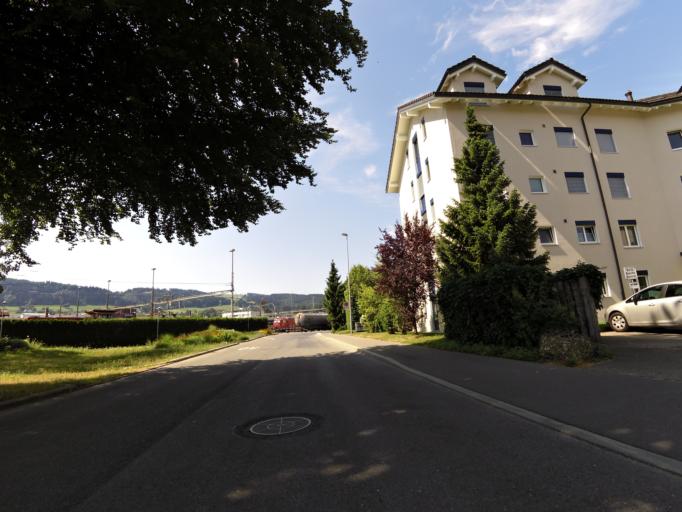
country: CH
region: Lucerne
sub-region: Lucerne-Land District
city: Meierskappel
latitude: 47.1433
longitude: 8.4321
